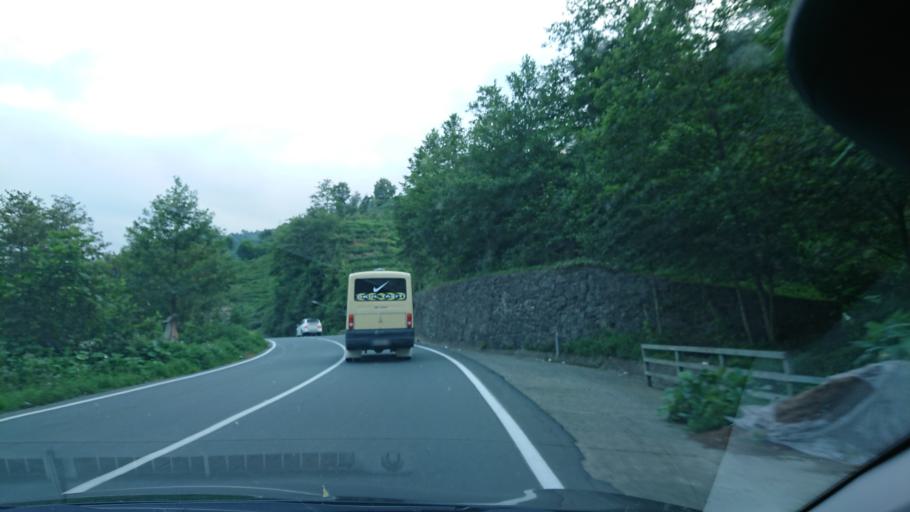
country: TR
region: Rize
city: Cayeli
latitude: 41.0736
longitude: 40.7112
